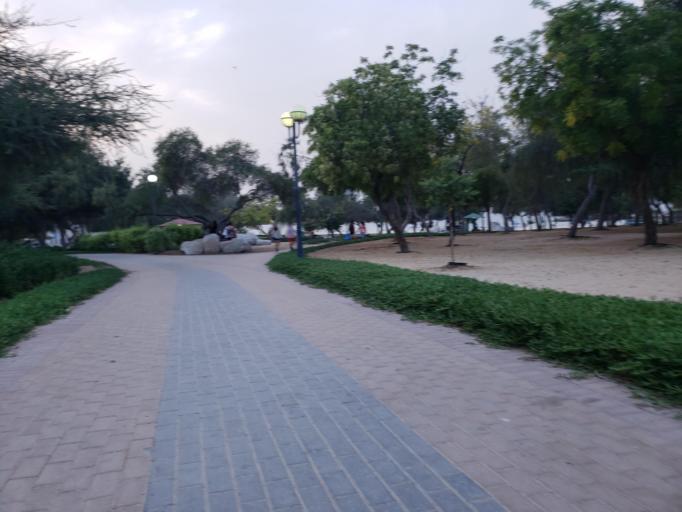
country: AE
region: Ash Shariqah
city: Sharjah
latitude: 25.3194
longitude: 55.3475
